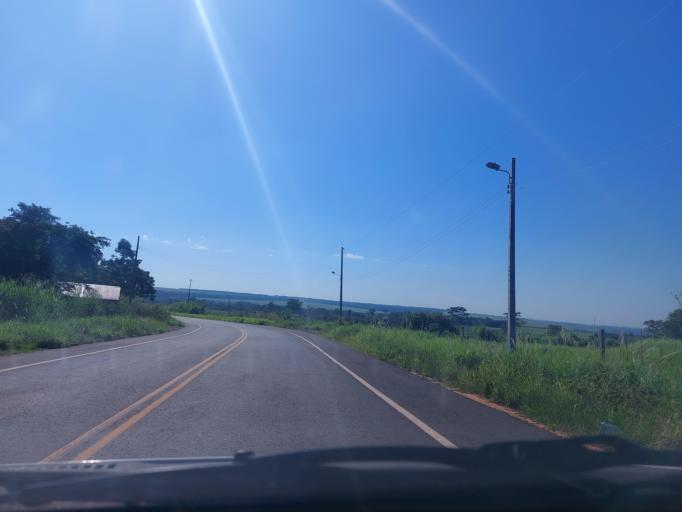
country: PY
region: San Pedro
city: Guayaybi
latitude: -24.3121
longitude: -56.1547
